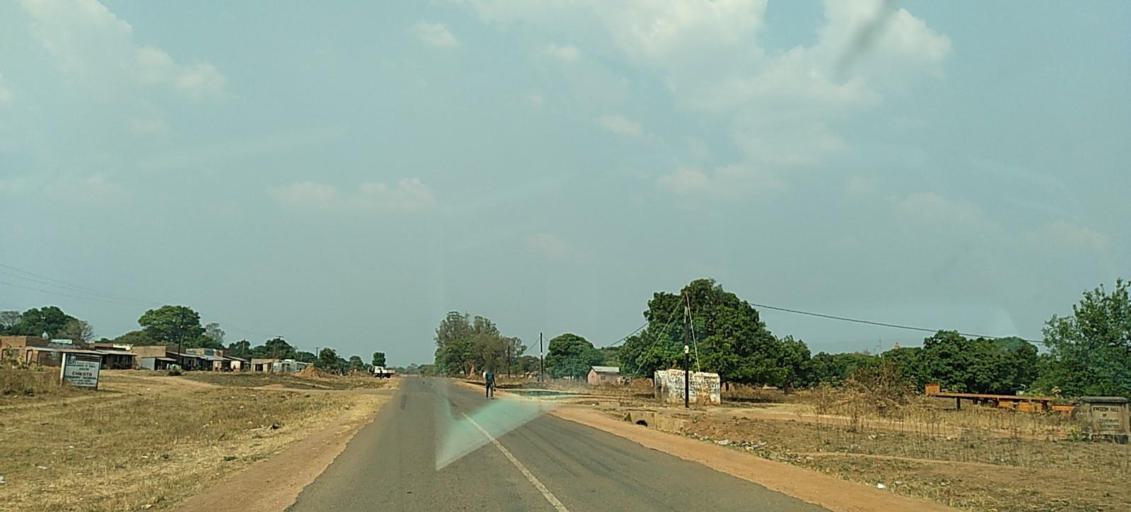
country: ZM
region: North-Western
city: Kabompo
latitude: -13.5893
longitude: 24.2240
